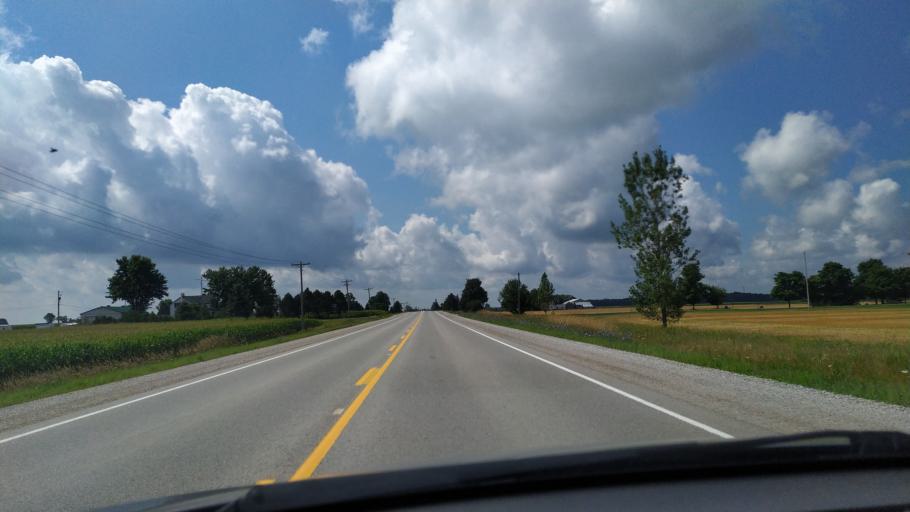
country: CA
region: Ontario
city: Huron East
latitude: 43.4153
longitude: -81.2428
